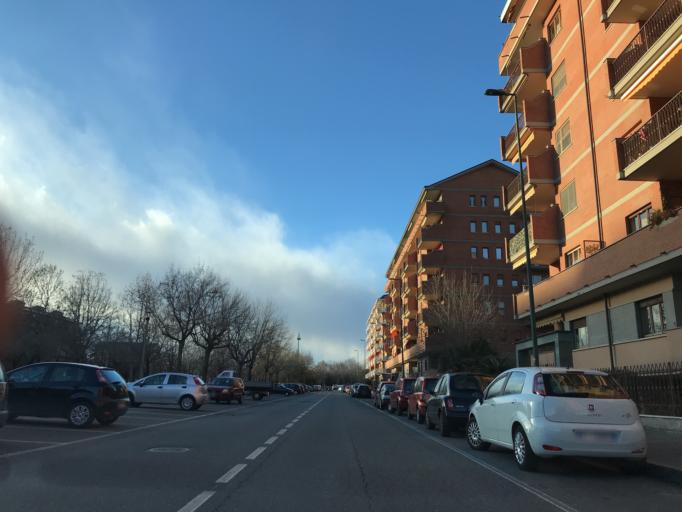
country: IT
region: Piedmont
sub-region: Provincia di Torino
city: Lesna
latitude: 45.0458
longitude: 7.6242
